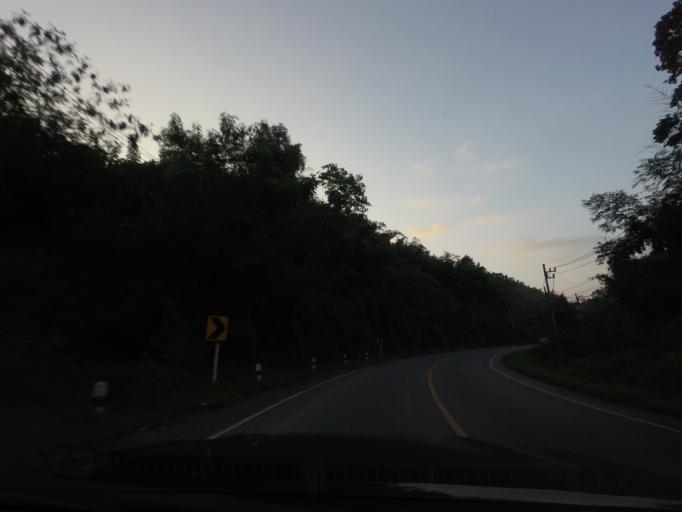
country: TH
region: Nan
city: Na Noi
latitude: 18.3881
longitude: 100.7082
